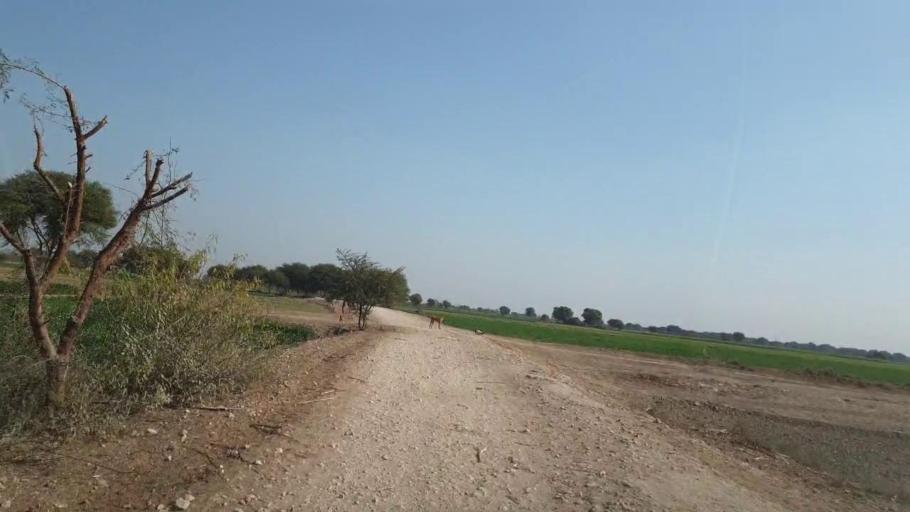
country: PK
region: Sindh
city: Matiari
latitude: 25.5098
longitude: 68.4833
